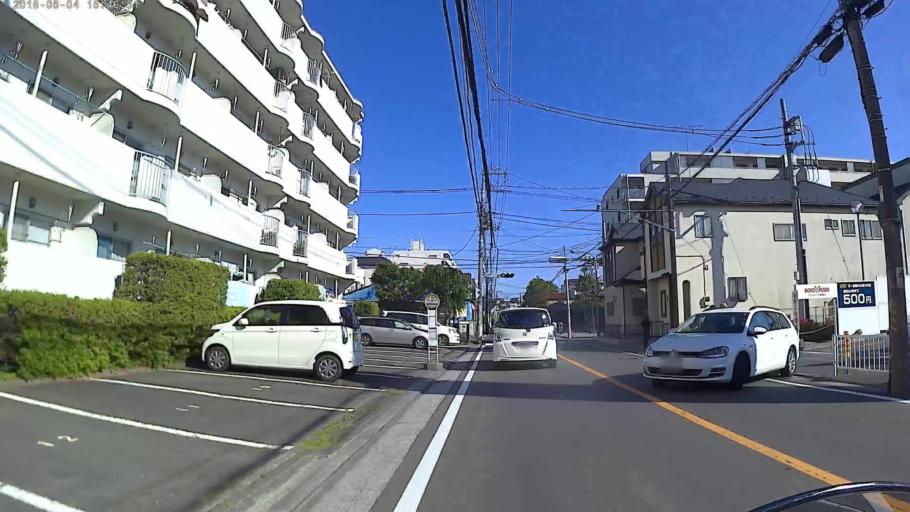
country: JP
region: Kanagawa
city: Yokohama
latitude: 35.5007
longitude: 139.6446
